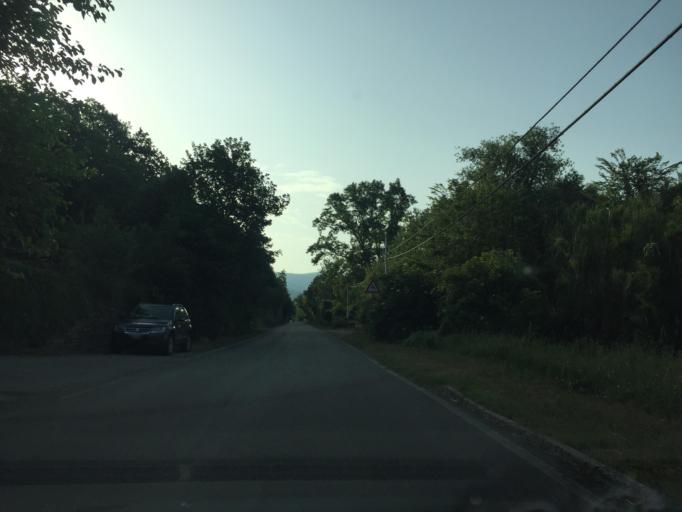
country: IT
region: Friuli Venezia Giulia
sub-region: Provincia di Trieste
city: Domio
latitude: 45.5890
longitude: 13.8160
